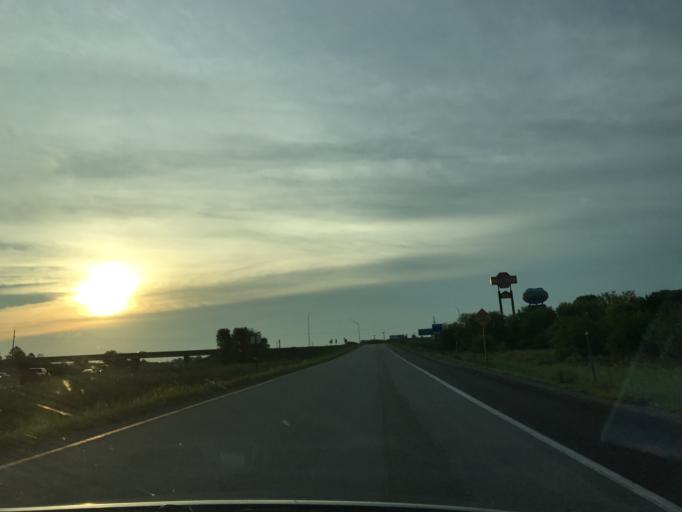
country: US
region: Iowa
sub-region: Iowa County
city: Williamsburg
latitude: 41.6875
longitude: -91.9142
